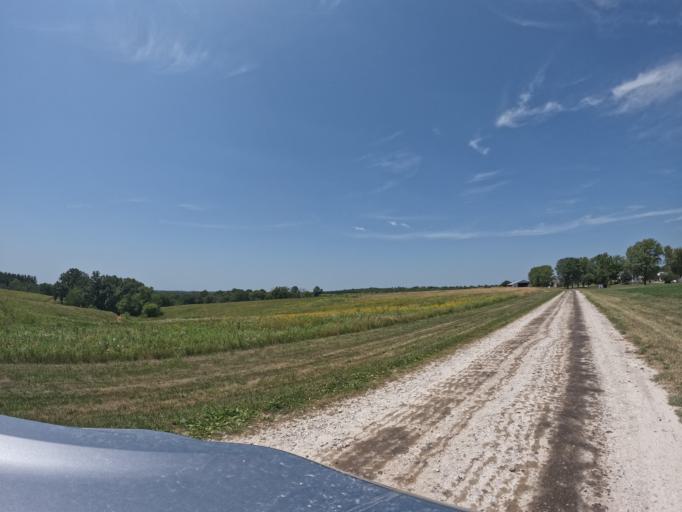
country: US
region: Iowa
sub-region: Henry County
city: Mount Pleasant
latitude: 40.9414
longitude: -91.5876
